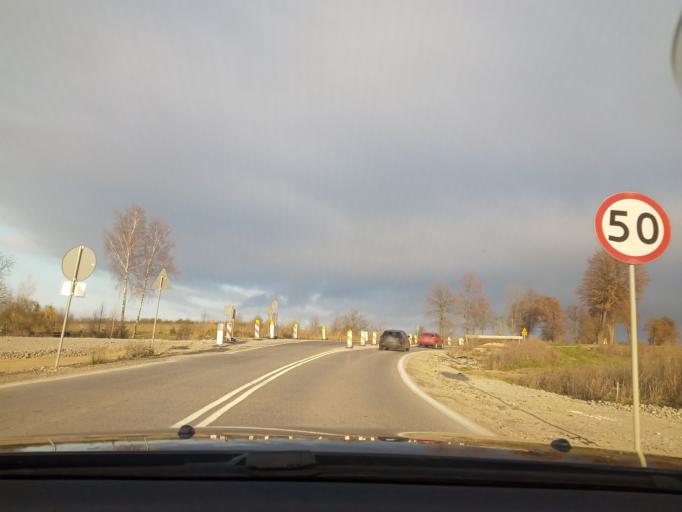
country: PL
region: Lesser Poland Voivodeship
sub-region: Powiat miechowski
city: Miechow
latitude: 50.3191
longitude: 20.0372
